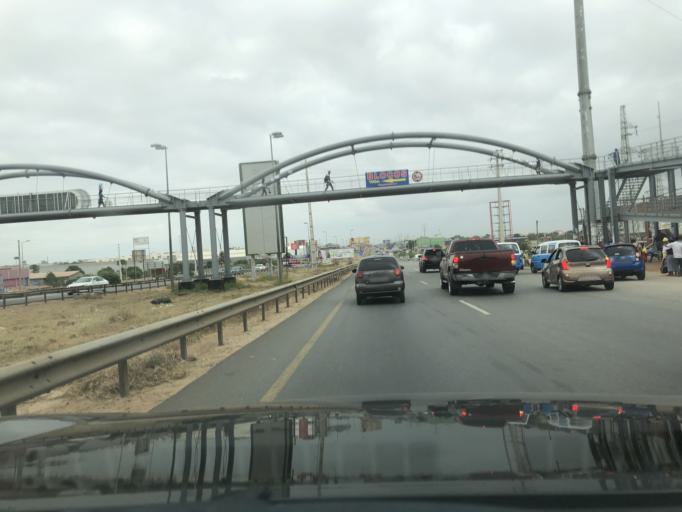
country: AO
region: Luanda
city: Luanda
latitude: -8.9748
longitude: 13.2114
